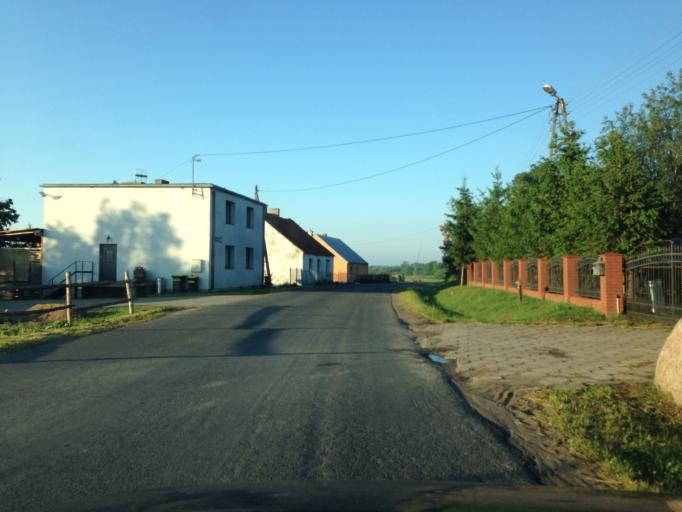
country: PL
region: Pomeranian Voivodeship
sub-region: Powiat tczewski
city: Gniew
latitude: 53.7769
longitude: 18.8319
